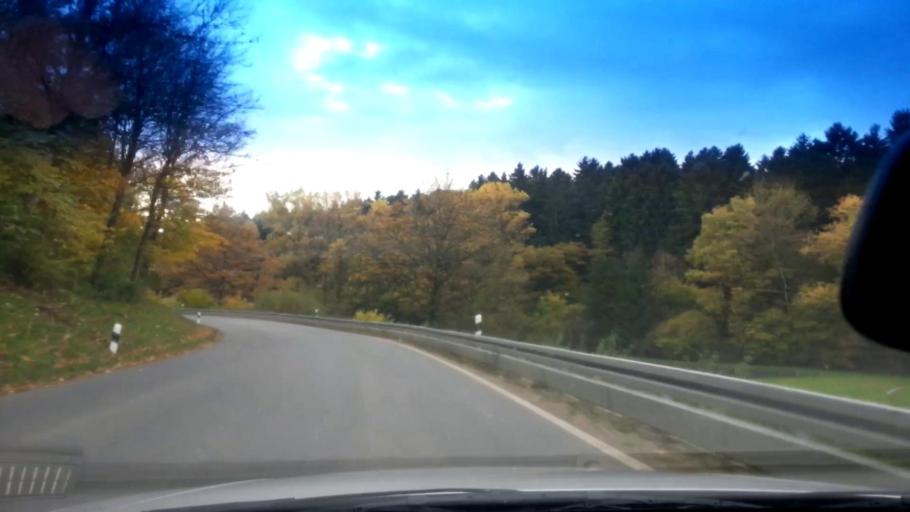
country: DE
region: Bavaria
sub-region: Upper Franconia
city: Wonsees
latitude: 49.9984
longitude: 11.2991
